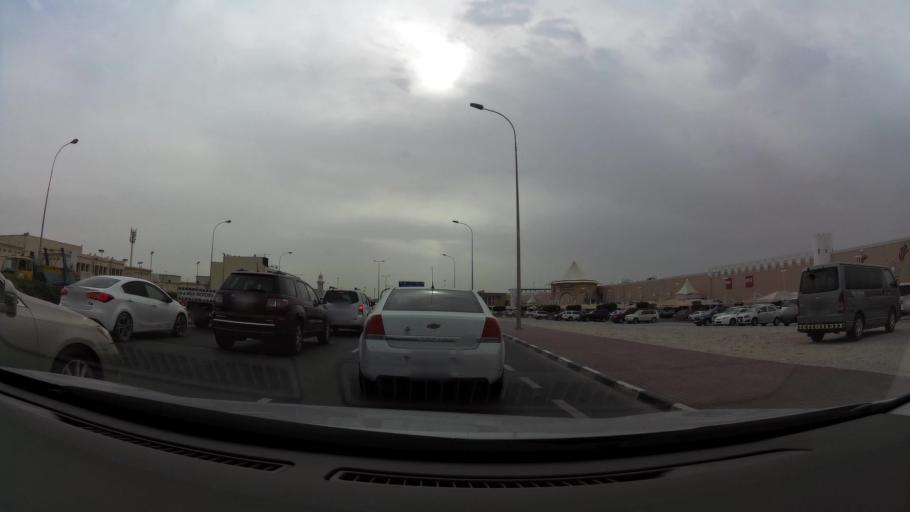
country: QA
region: Baladiyat ar Rayyan
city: Ar Rayyan
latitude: 25.3334
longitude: 51.4680
